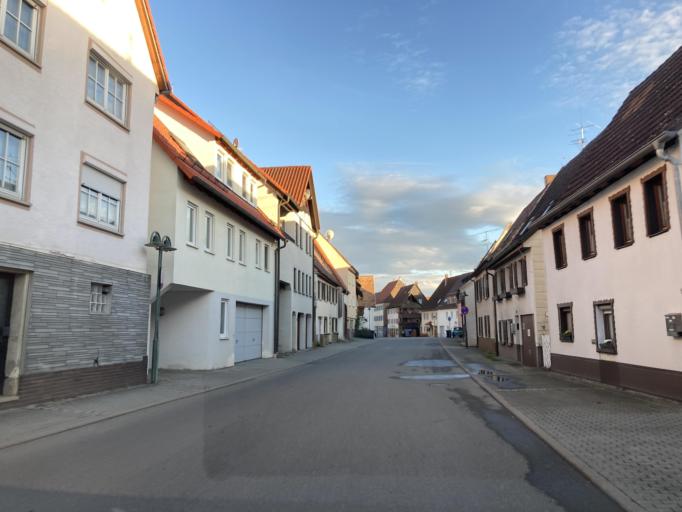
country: DE
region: Baden-Wuerttemberg
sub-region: Regierungsbezirk Stuttgart
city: Motzingen
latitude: 48.5064
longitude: 8.7717
